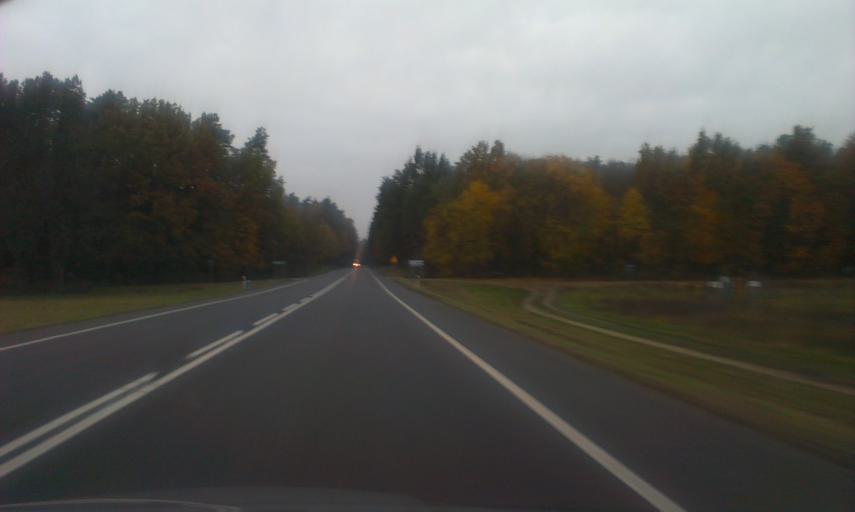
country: PL
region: Greater Poland Voivodeship
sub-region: Powiat chodzieski
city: Chodziez
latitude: 52.9978
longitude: 16.8683
